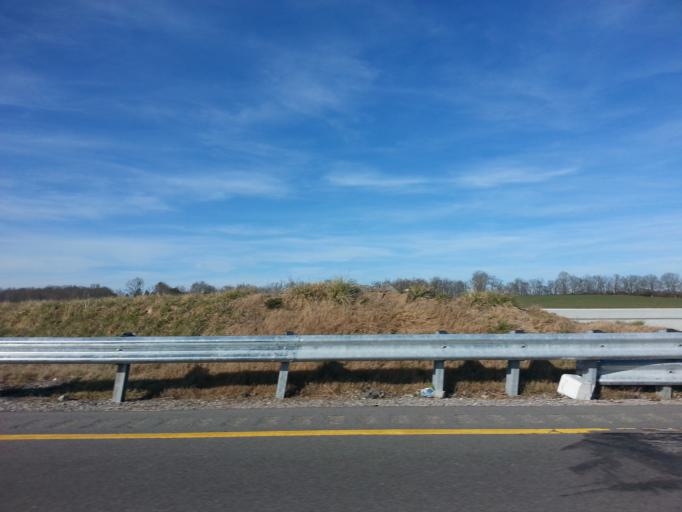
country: US
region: Tennessee
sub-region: Warren County
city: McMinnville
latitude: 35.7300
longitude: -85.9121
